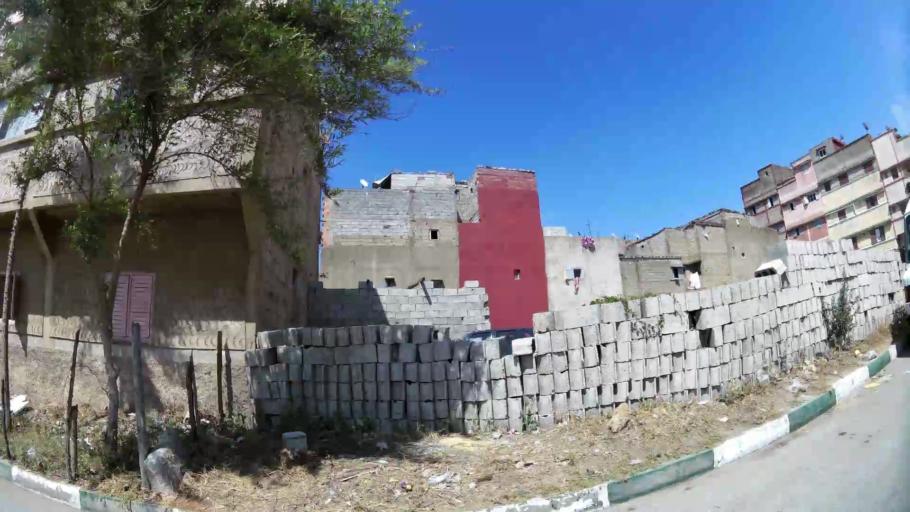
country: MA
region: Rabat-Sale-Zemmour-Zaer
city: Sale
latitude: 34.0623
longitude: -6.7773
